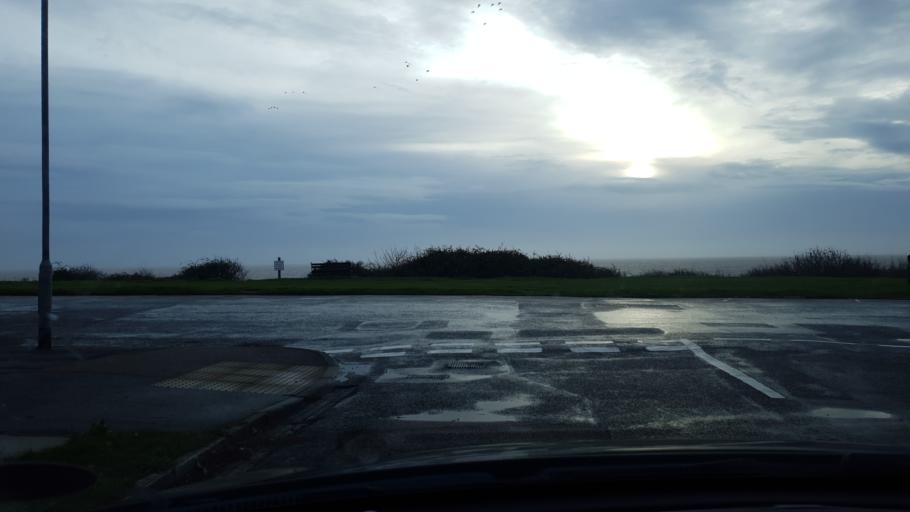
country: GB
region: England
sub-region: Essex
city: Frinton-on-Sea
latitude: 51.8339
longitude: 1.2526
